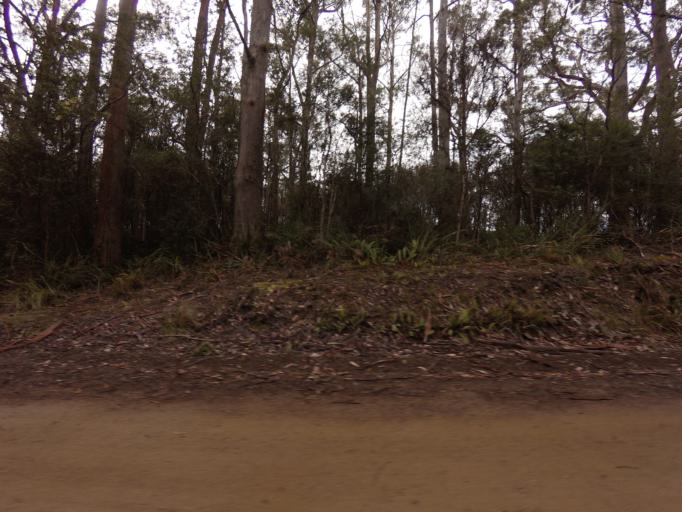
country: AU
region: Tasmania
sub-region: Huon Valley
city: Geeveston
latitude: -43.5441
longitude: 146.8901
